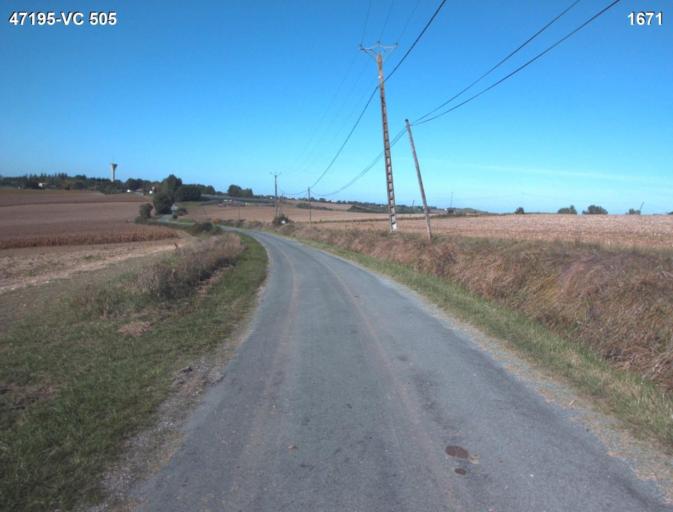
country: FR
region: Aquitaine
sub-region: Departement du Lot-et-Garonne
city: Nerac
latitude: 44.1453
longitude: 0.3797
